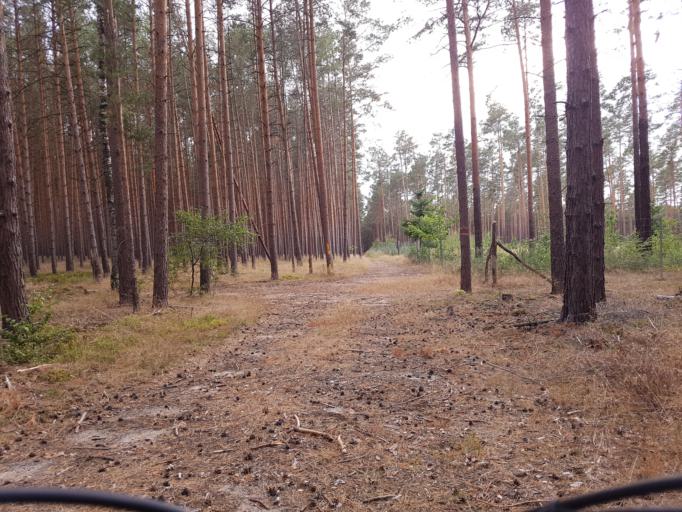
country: DE
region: Brandenburg
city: Trobitz
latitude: 51.5649
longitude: 13.4380
